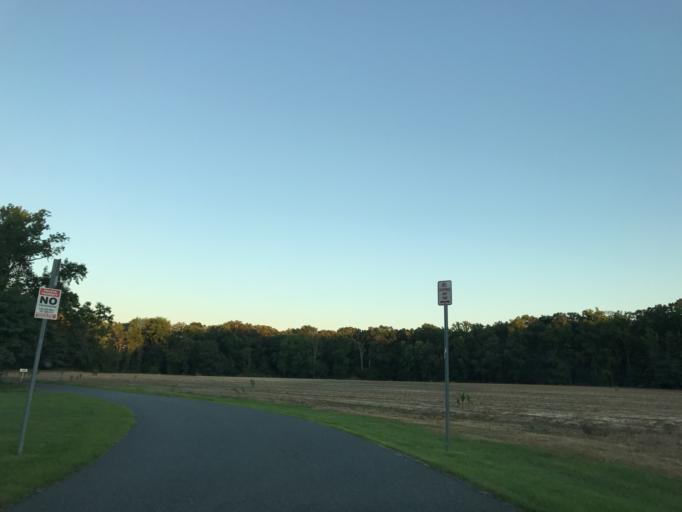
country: US
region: Maryland
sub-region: Baltimore County
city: Bowleys Quarters
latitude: 39.3394
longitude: -76.3793
